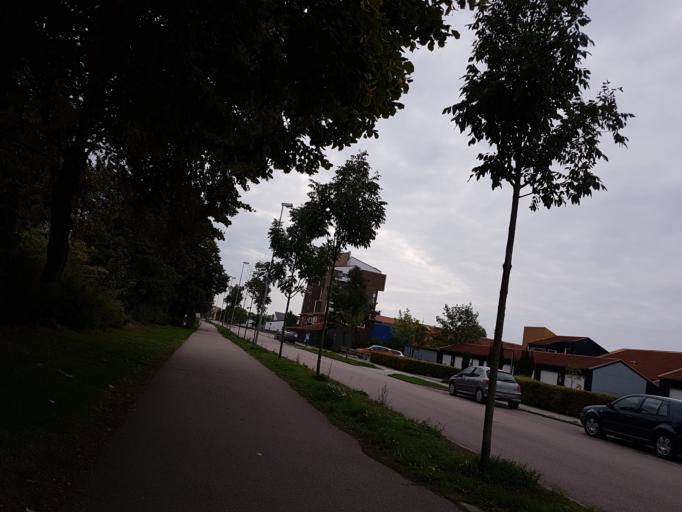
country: SE
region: Skane
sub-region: Landskrona
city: Landskrona
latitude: 55.8907
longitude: 12.8251
